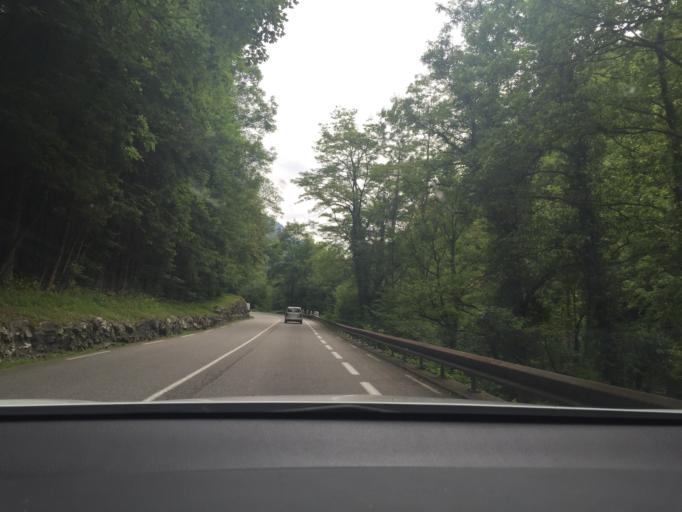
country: FR
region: Rhone-Alpes
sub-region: Departement de la Savoie
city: Vimines
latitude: 45.5243
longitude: 5.8551
